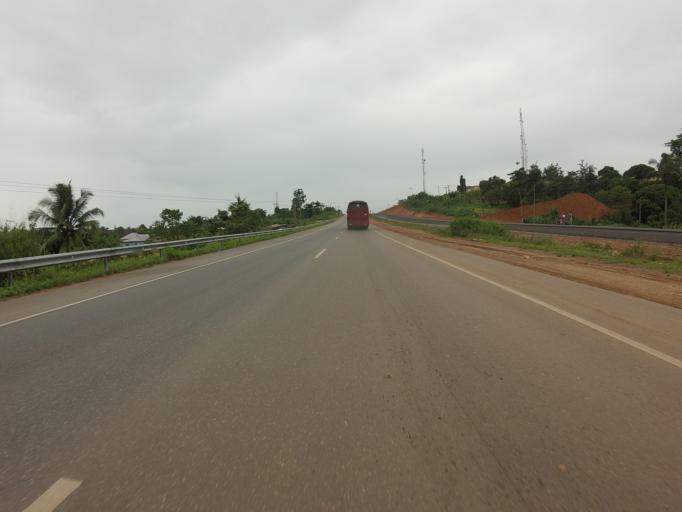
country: GH
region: Eastern
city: Suhum
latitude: 6.0460
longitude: -0.4599
